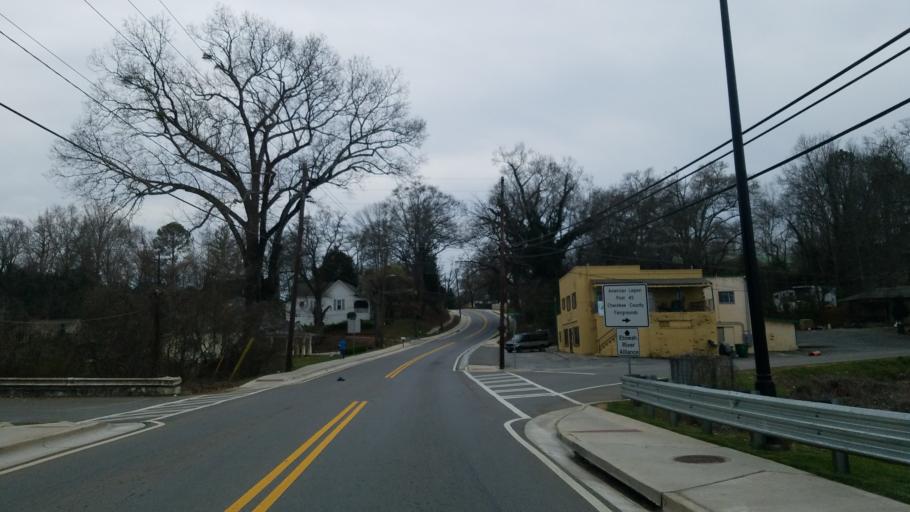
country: US
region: Georgia
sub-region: Cherokee County
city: Canton
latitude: 34.2271
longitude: -84.4930
